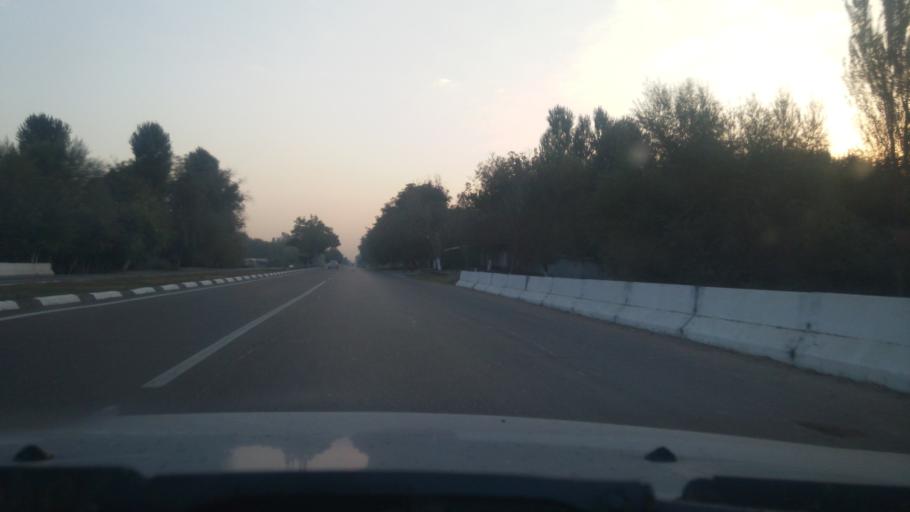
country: UZ
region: Toshkent
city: Amir Timur
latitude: 41.0635
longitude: 68.9140
